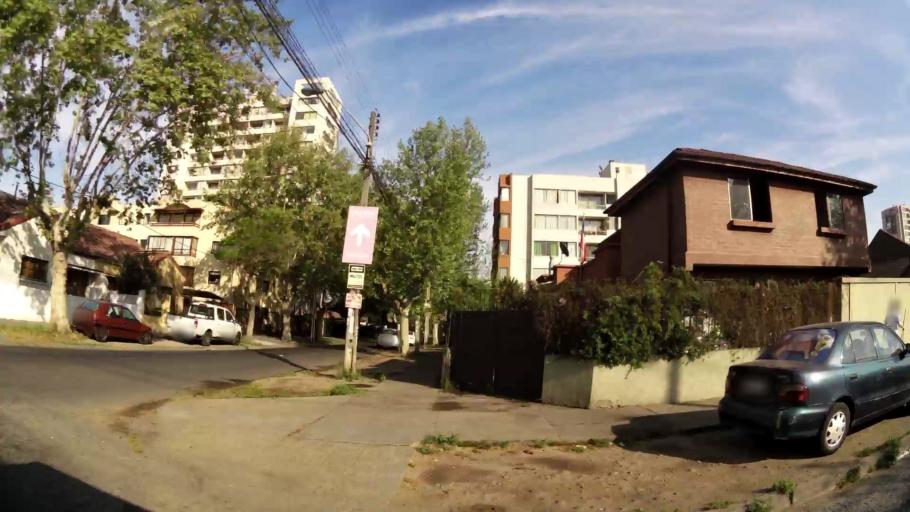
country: CL
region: Santiago Metropolitan
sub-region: Provincia de Santiago
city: Santiago
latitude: -33.5097
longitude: -70.6597
